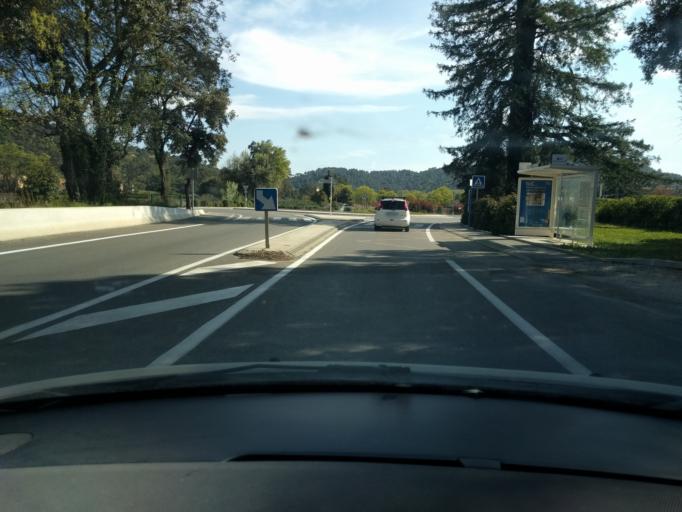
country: FR
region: Provence-Alpes-Cote d'Azur
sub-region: Departement du Var
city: La Crau
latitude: 43.1730
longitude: 6.1180
